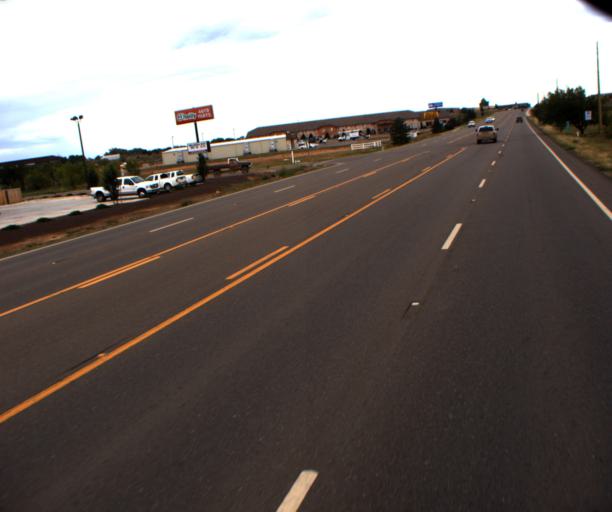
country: US
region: Arizona
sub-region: Navajo County
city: Taylor
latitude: 34.4834
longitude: -110.0836
